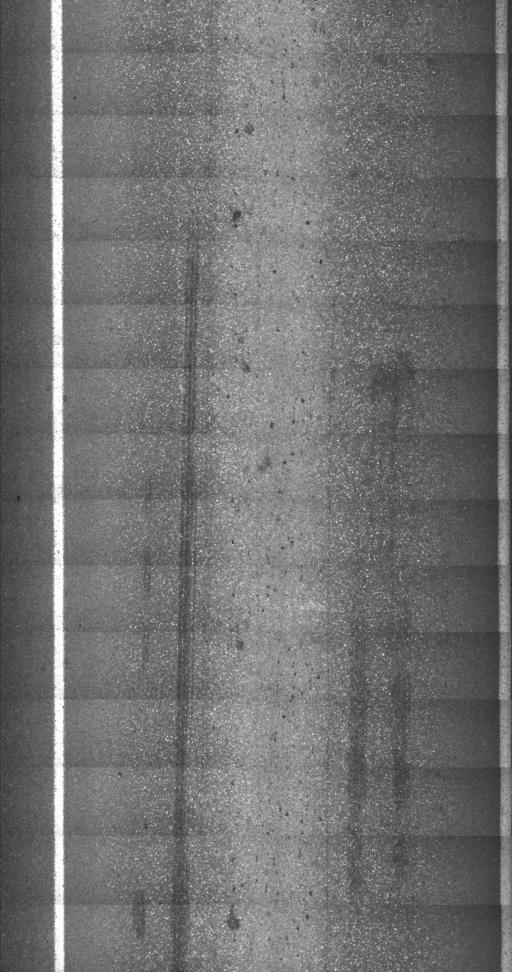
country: US
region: Vermont
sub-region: Chittenden County
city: Essex Junction
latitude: 44.5149
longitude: -73.1221
